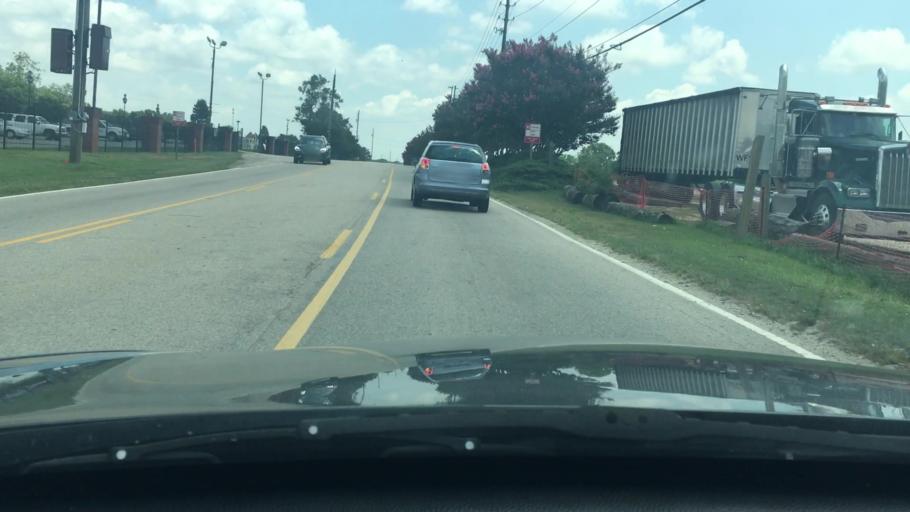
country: US
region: North Carolina
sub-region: Wake County
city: West Raleigh
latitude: 35.7922
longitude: -78.7112
